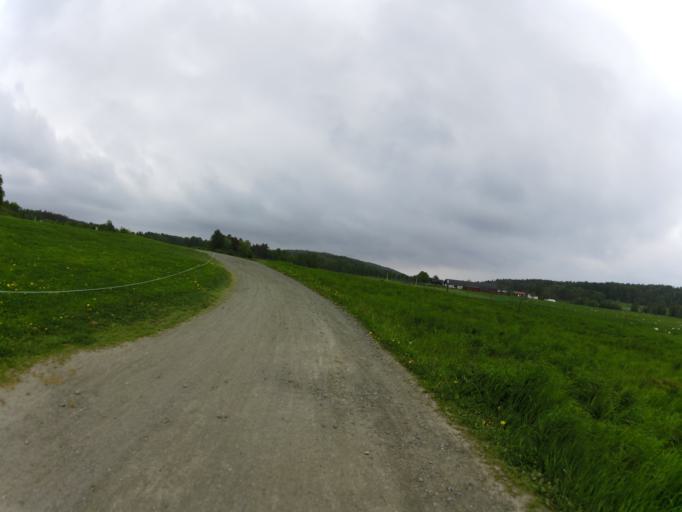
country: NO
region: Ostfold
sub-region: Rygge
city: Larkollen
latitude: 59.3732
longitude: 10.6799
